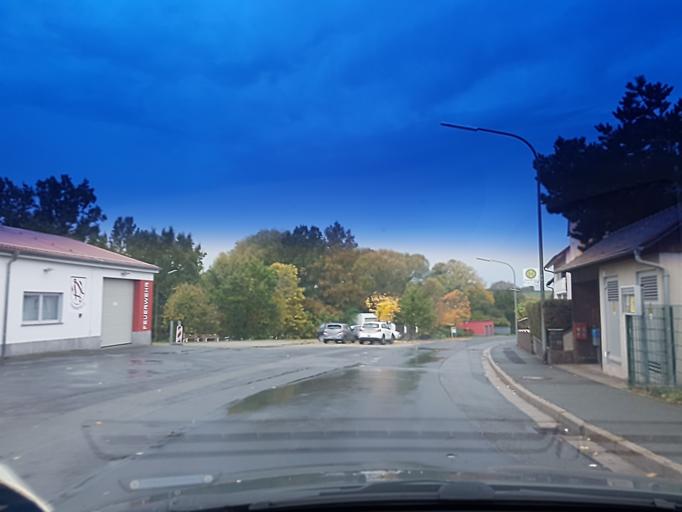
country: DE
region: Bavaria
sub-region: Upper Franconia
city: Schlusselfeld
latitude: 49.7534
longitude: 10.6325
